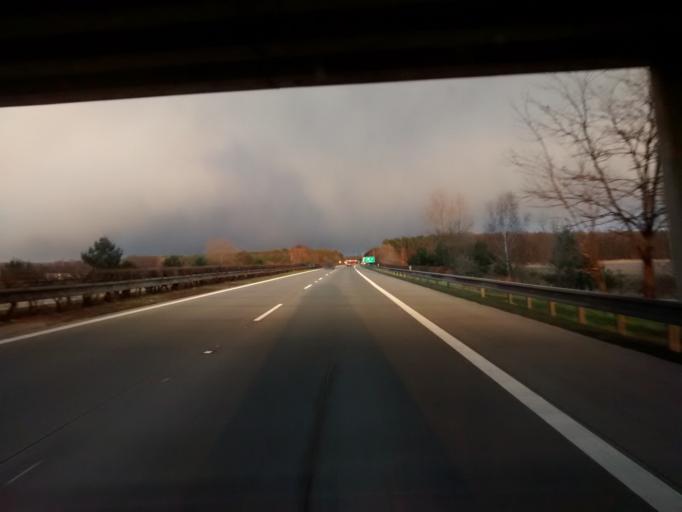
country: CZ
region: Central Bohemia
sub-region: Okres Nymburk
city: Podebrady
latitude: 50.1203
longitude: 15.1019
